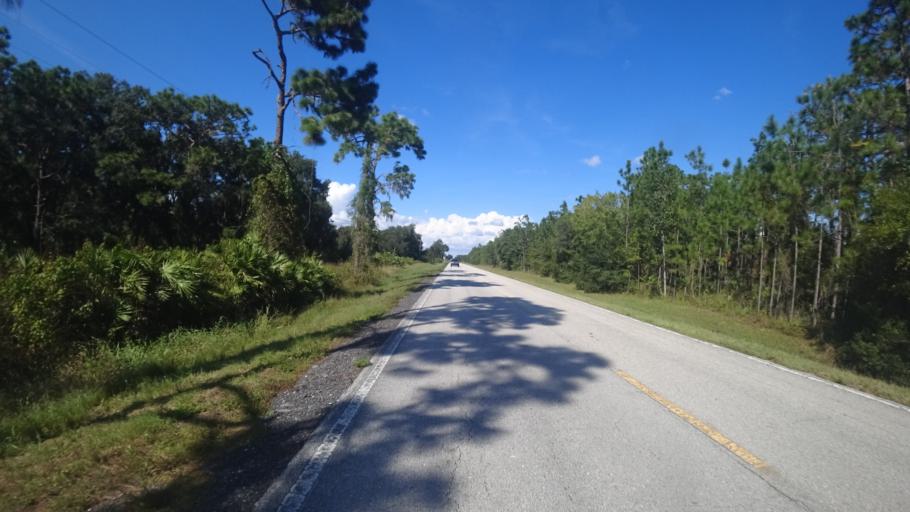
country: US
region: Florida
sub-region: Sarasota County
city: The Meadows
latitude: 27.4387
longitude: -82.3035
